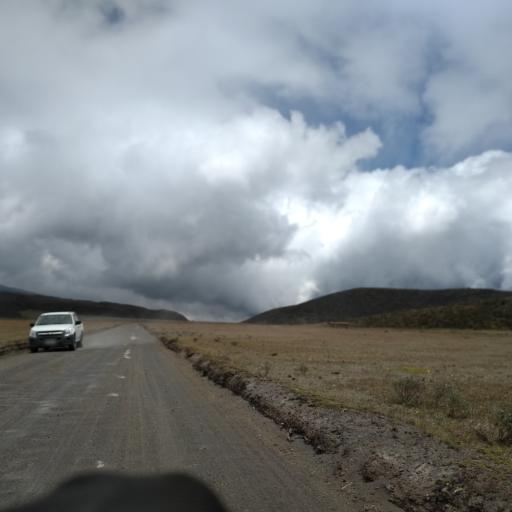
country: EC
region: Pichincha
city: Machachi
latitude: -0.6153
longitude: -78.4734
